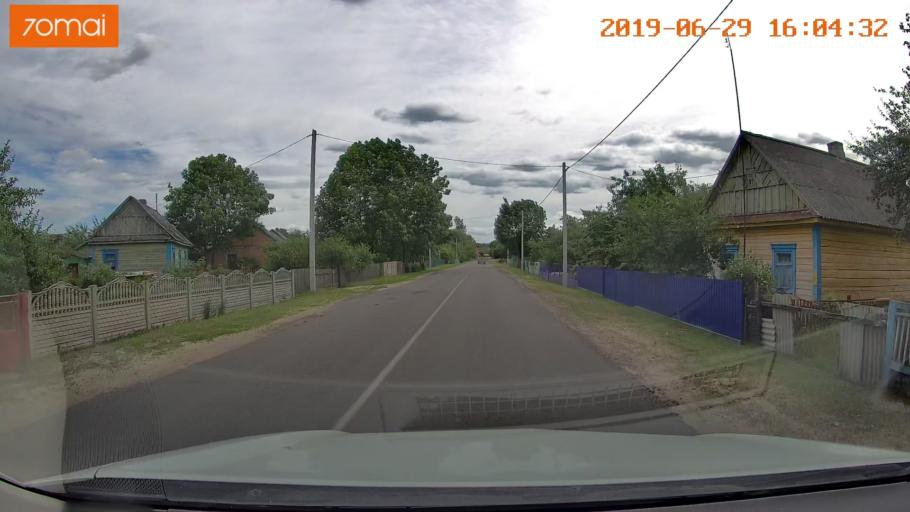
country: BY
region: Brest
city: Luninyets
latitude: 52.2218
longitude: 27.0250
